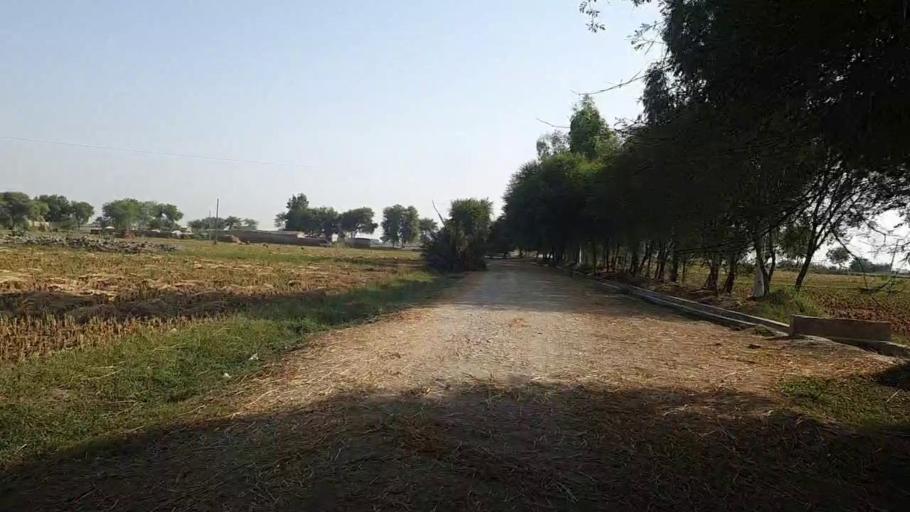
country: PK
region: Sindh
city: Kandhkot
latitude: 28.3527
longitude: 69.3352
